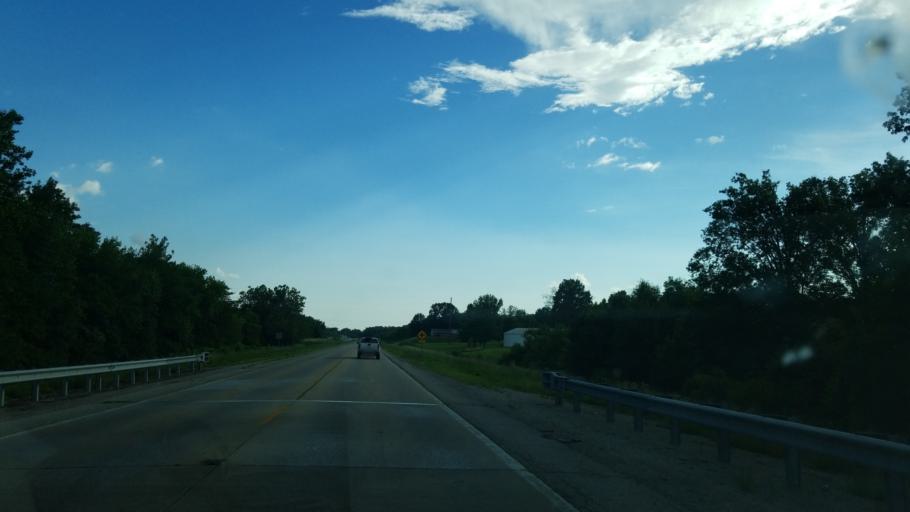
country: US
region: Illinois
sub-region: Marion County
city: Central City
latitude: 38.5628
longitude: -89.1197
